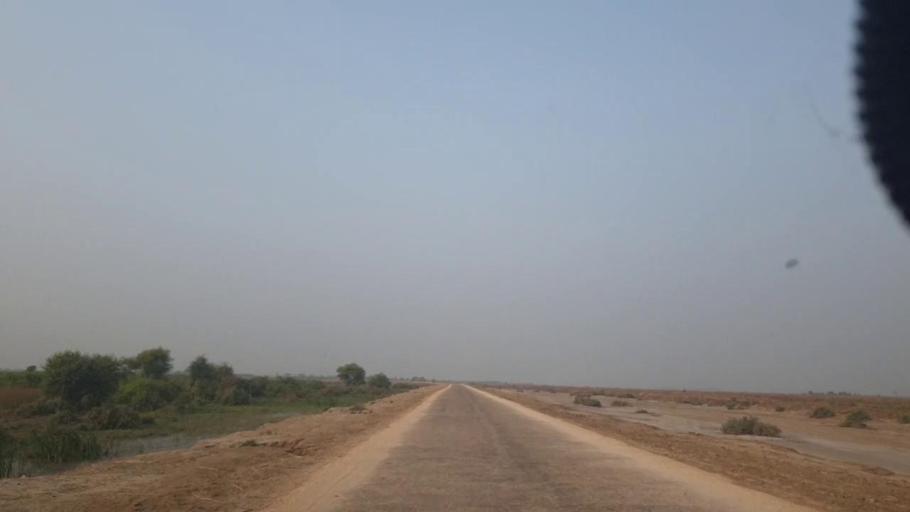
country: PK
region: Sindh
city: Bulri
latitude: 24.8481
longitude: 68.4045
